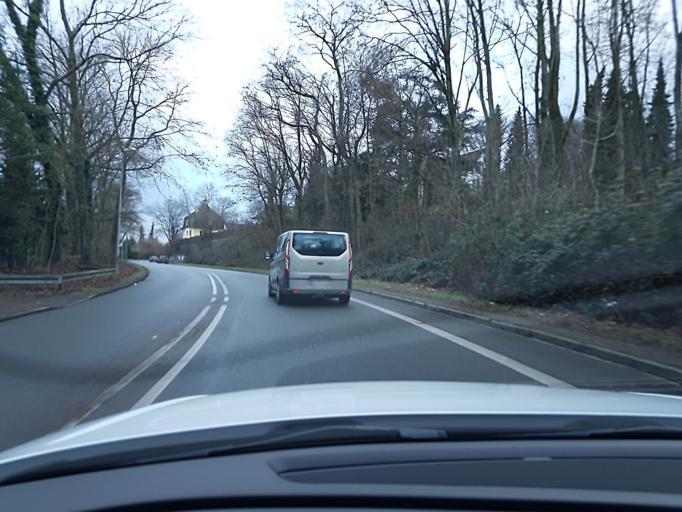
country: DE
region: North Rhine-Westphalia
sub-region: Regierungsbezirk Dusseldorf
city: Muelheim (Ruhr)
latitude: 51.4109
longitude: 6.8946
